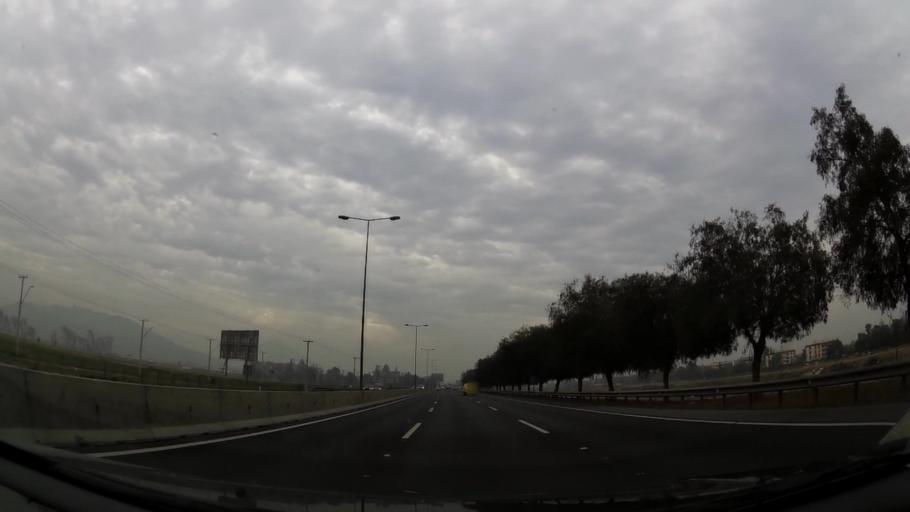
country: CL
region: Santiago Metropolitan
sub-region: Provincia de Santiago
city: Lo Prado
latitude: -33.4120
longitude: -70.7542
